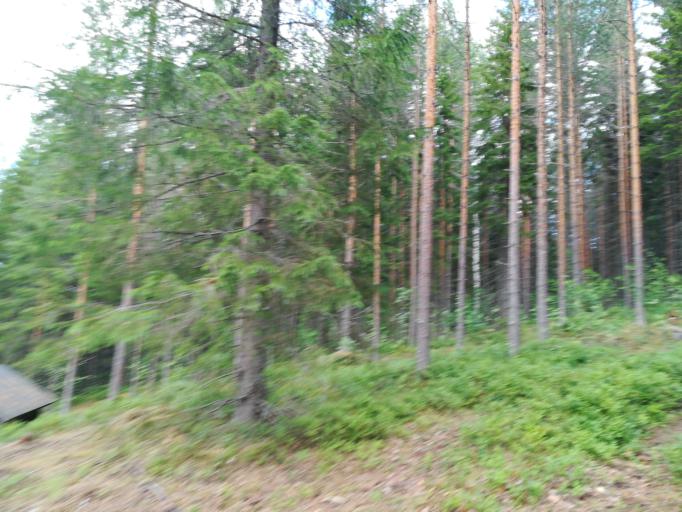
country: FI
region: South Karelia
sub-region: Lappeenranta
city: Savitaipale
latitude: 61.3035
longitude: 27.6117
